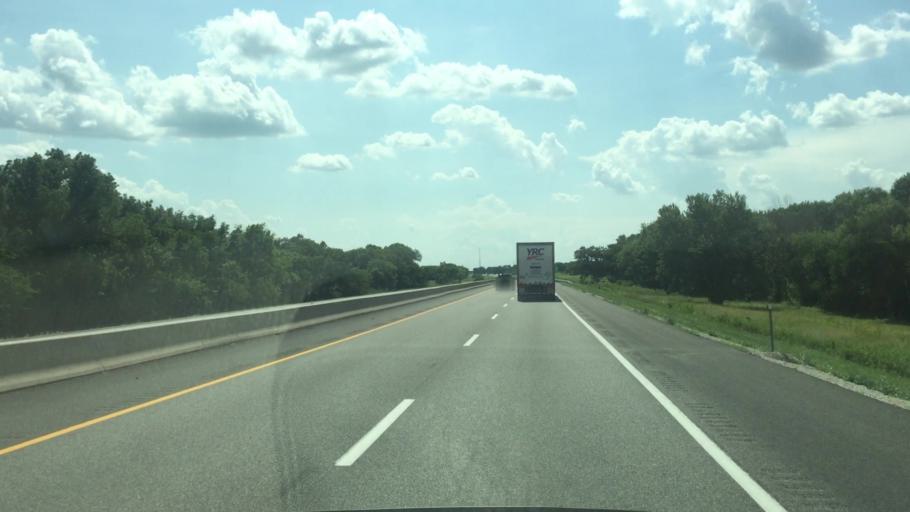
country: US
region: Kansas
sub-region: Butler County
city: Andover
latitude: 37.7306
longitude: -97.0879
